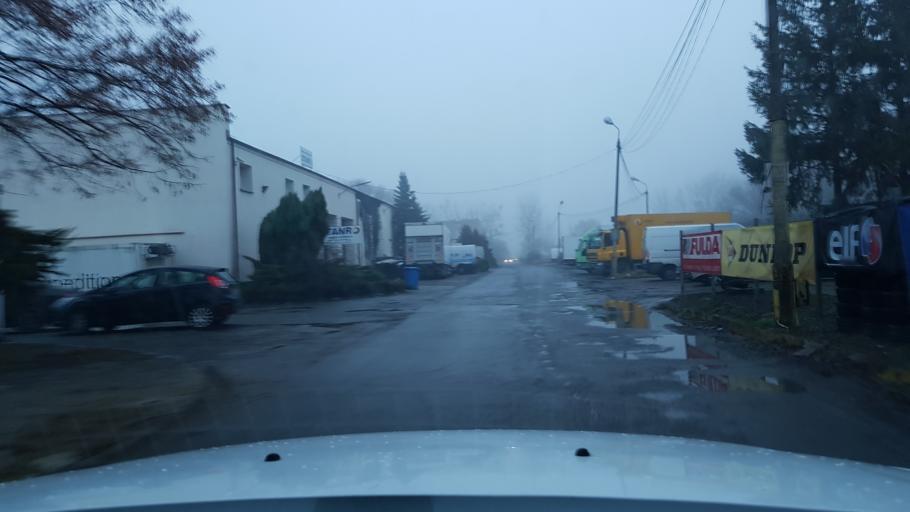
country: PL
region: West Pomeranian Voivodeship
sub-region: Powiat policki
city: Przeclaw
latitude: 53.3893
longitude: 14.4946
